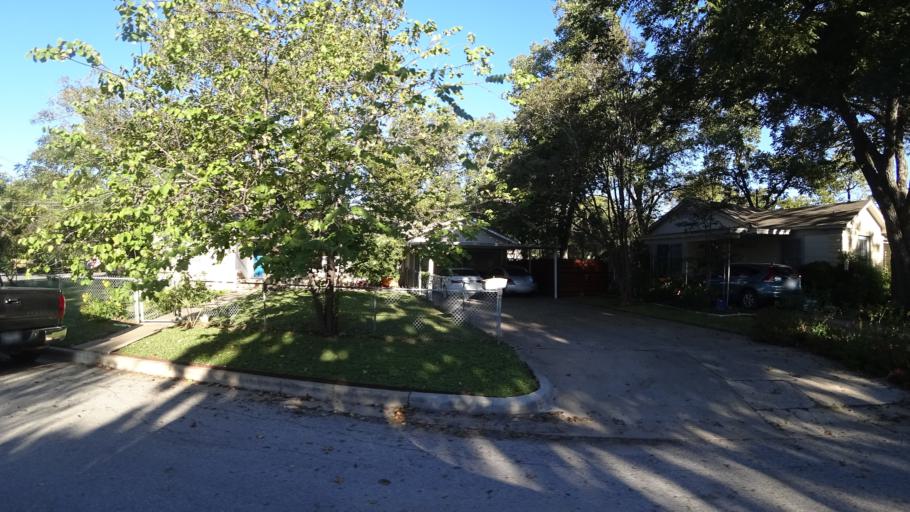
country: US
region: Texas
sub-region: Travis County
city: Austin
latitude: 30.3087
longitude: -97.7204
